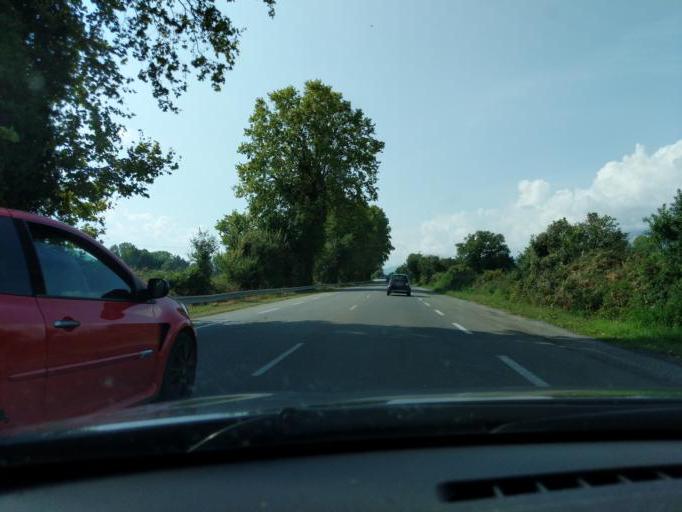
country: FR
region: Corsica
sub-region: Departement de la Haute-Corse
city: Ghisonaccia
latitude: 41.9796
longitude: 9.4000
